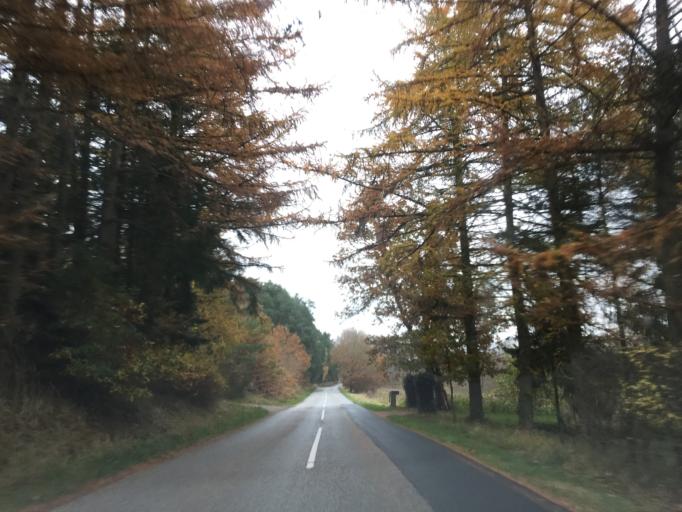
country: DK
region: Central Jutland
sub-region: Silkeborg Kommune
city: Svejbaek
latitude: 56.2046
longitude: 9.6495
